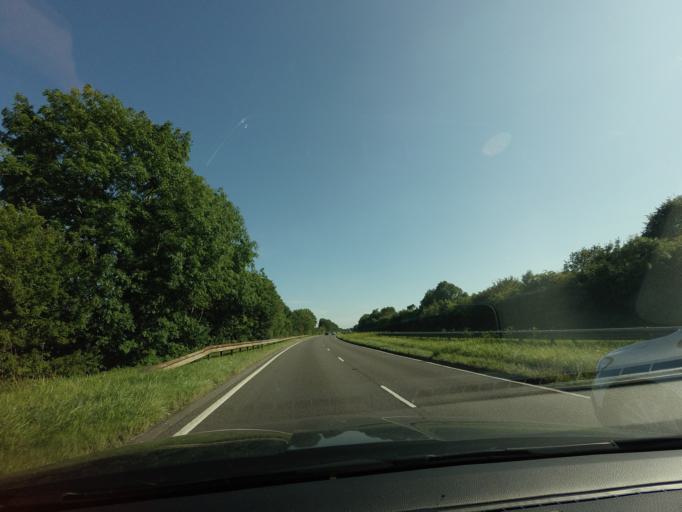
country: GB
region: England
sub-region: Derbyshire
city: Chesterfield
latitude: 53.2226
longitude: -1.3996
